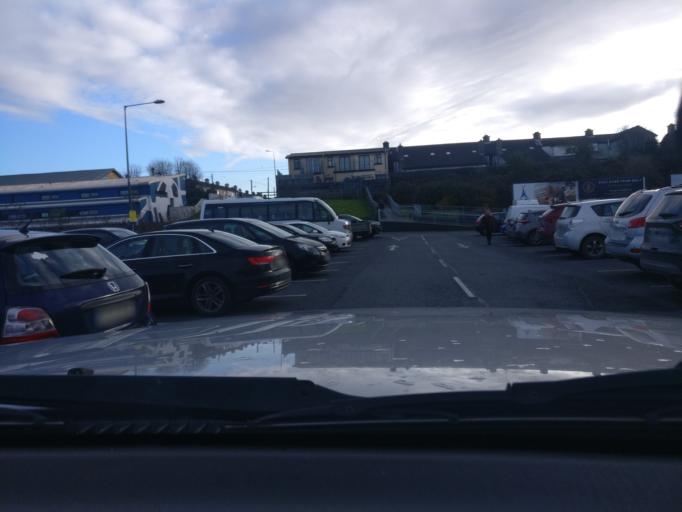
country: IE
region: Connaught
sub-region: County Galway
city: Gaillimh
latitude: 53.2812
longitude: -9.0461
